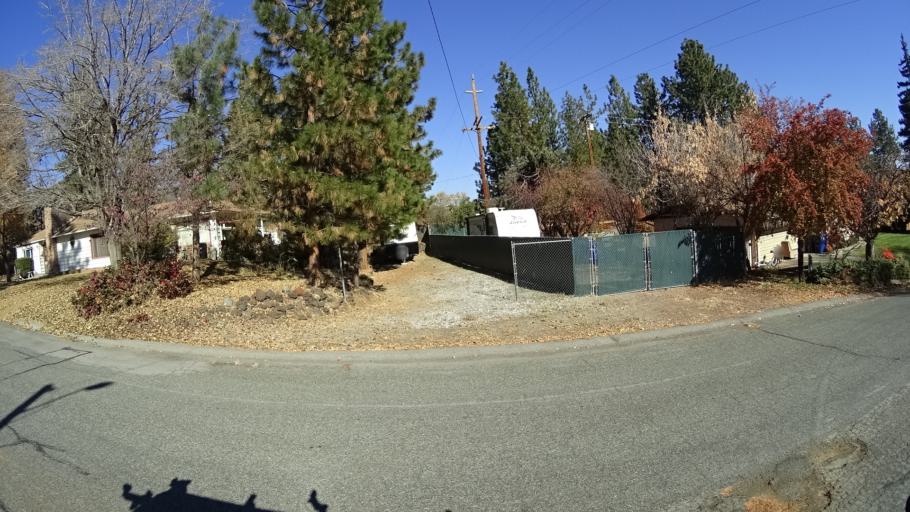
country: US
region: California
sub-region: Siskiyou County
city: Yreka
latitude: 41.7393
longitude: -122.6474
